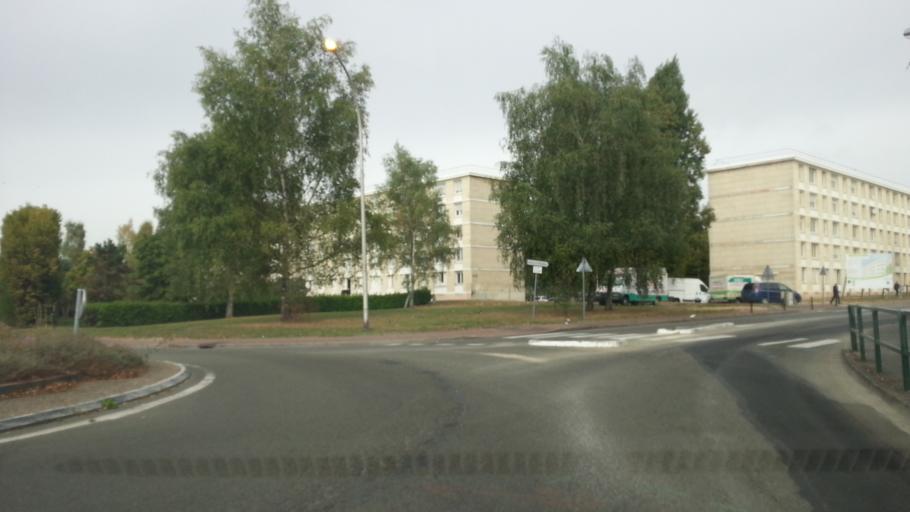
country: FR
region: Picardie
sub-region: Departement de l'Oise
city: Creil
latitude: 49.2489
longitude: 2.4676
